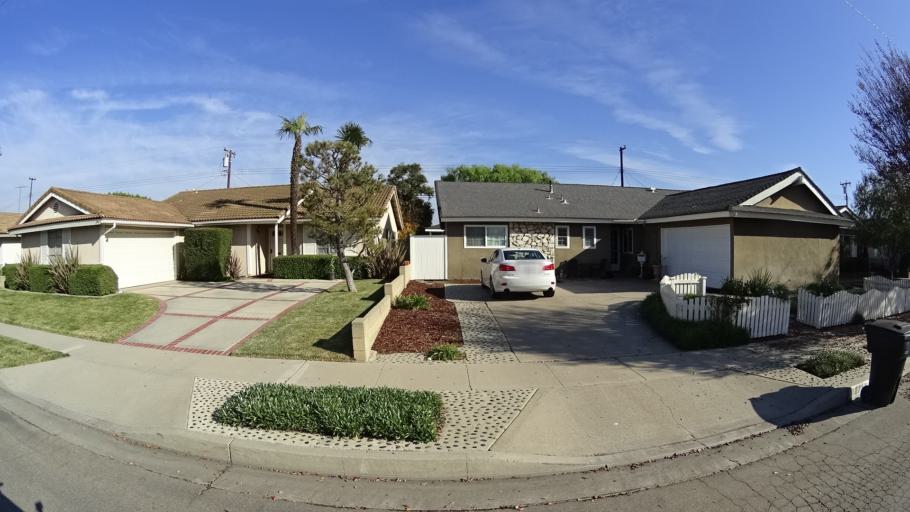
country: US
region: California
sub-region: Orange County
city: Westminster
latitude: 33.7777
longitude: -118.0298
